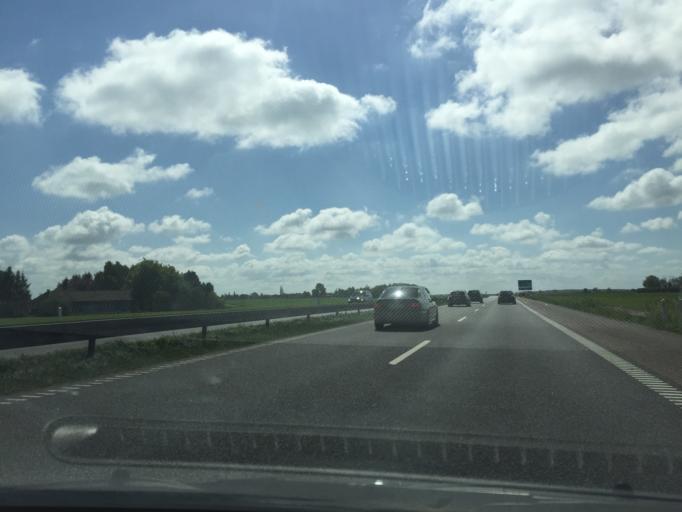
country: DK
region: Zealand
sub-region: Vordingborg Kommune
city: Nyrad
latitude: 54.9315
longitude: 11.9547
